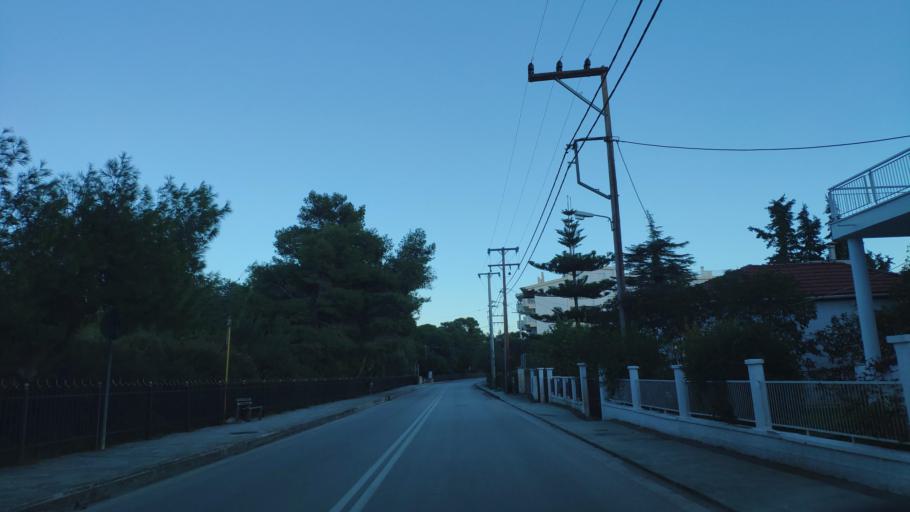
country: GR
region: Peloponnese
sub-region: Nomos Korinthias
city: Xylokastro
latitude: 38.0725
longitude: 22.6455
